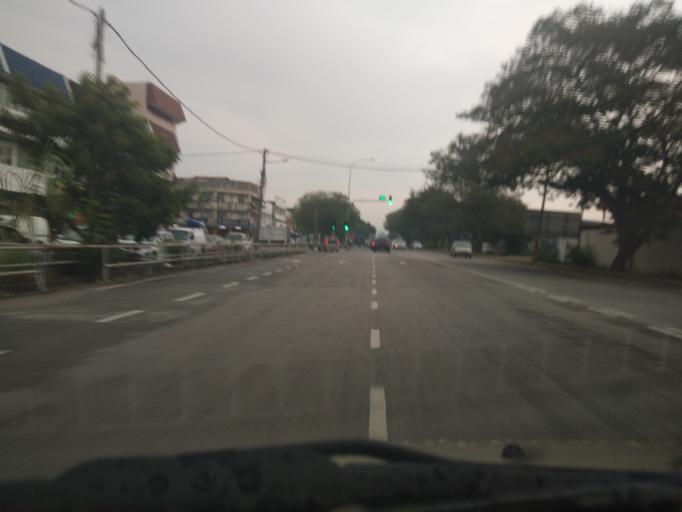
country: MY
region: Penang
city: Permatang Kuching
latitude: 5.4495
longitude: 100.3990
